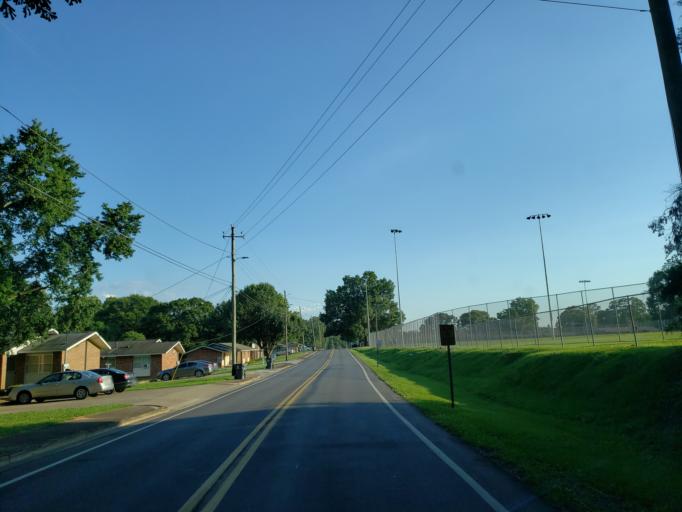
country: US
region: Georgia
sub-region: Haralson County
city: Tallapoosa
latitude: 33.7535
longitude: -85.2953
